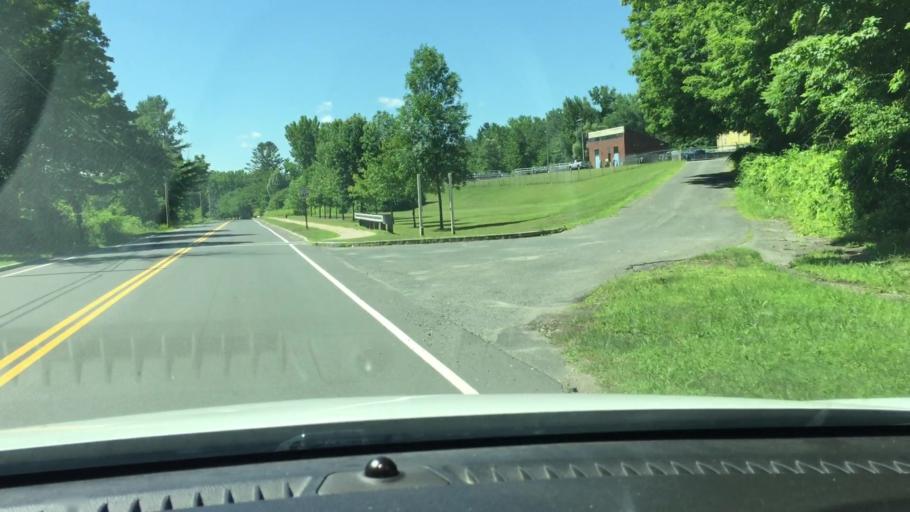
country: US
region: Massachusetts
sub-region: Berkshire County
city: Lenox
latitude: 42.3496
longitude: -73.2451
